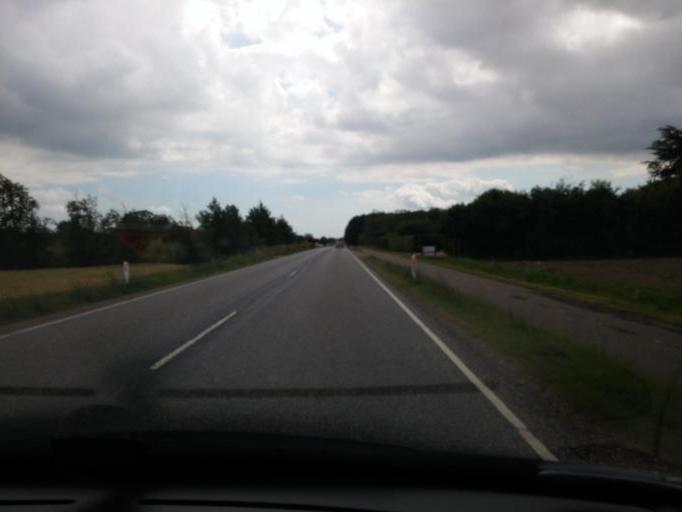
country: DK
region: South Denmark
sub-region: Svendborg Kommune
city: Vindeby
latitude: 55.0143
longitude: 10.6082
